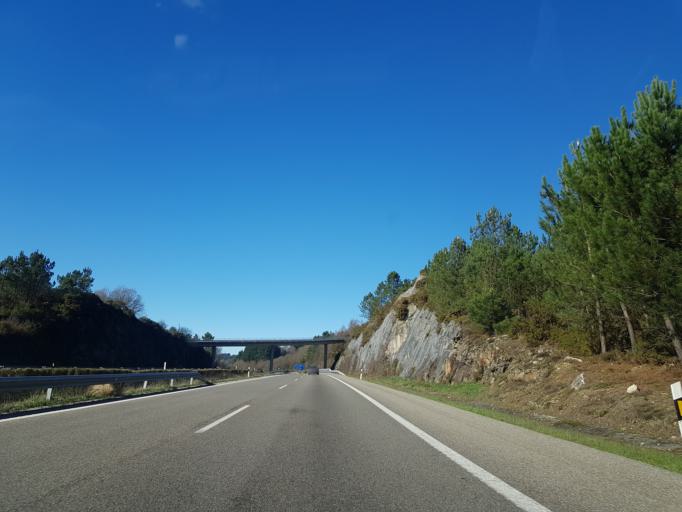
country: ES
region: Galicia
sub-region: Provincia de Lugo
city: Guitiriz
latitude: 43.1767
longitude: -7.8009
